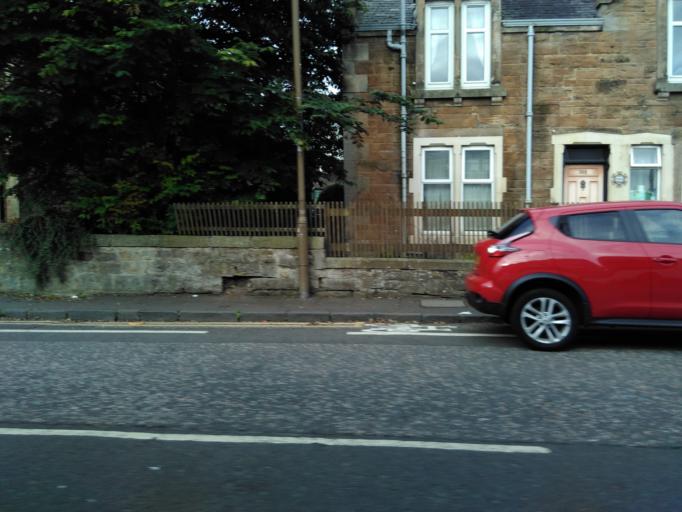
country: GB
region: Scotland
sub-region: Midlothian
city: Loanhead
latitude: 55.9146
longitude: -3.1487
